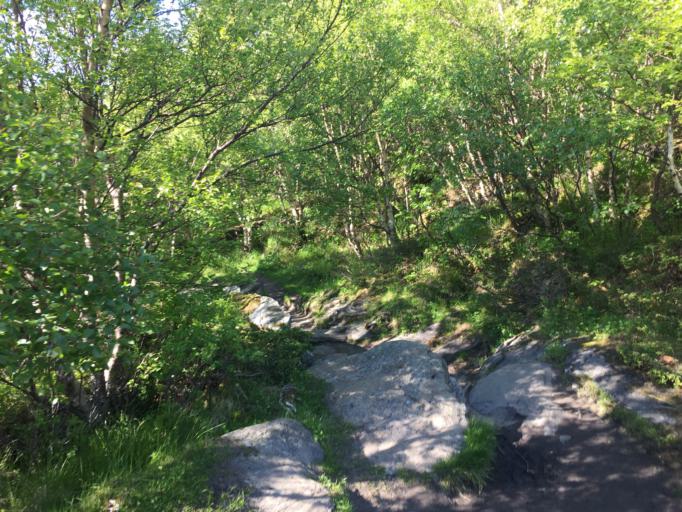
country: NO
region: Nordland
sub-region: Bodo
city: Loding
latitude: 67.4163
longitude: 14.6325
